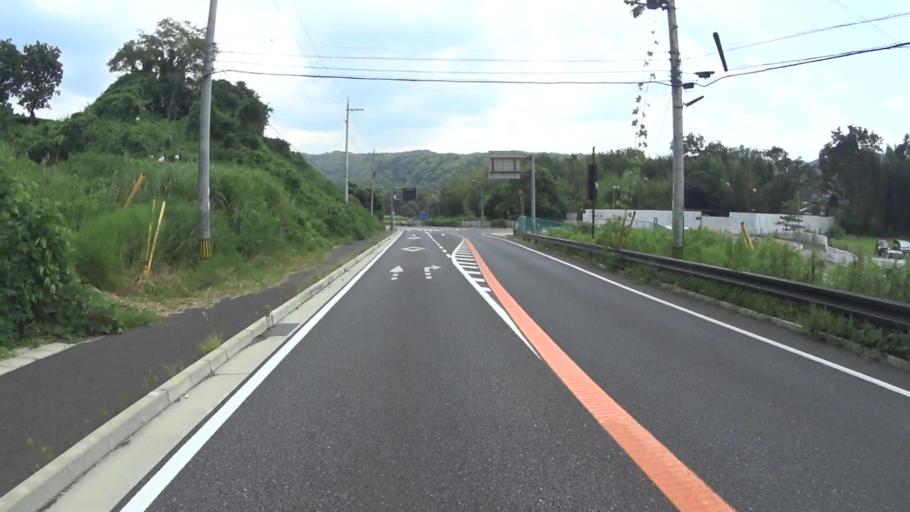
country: JP
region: Nara
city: Nara-shi
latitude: 34.7656
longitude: 135.8813
